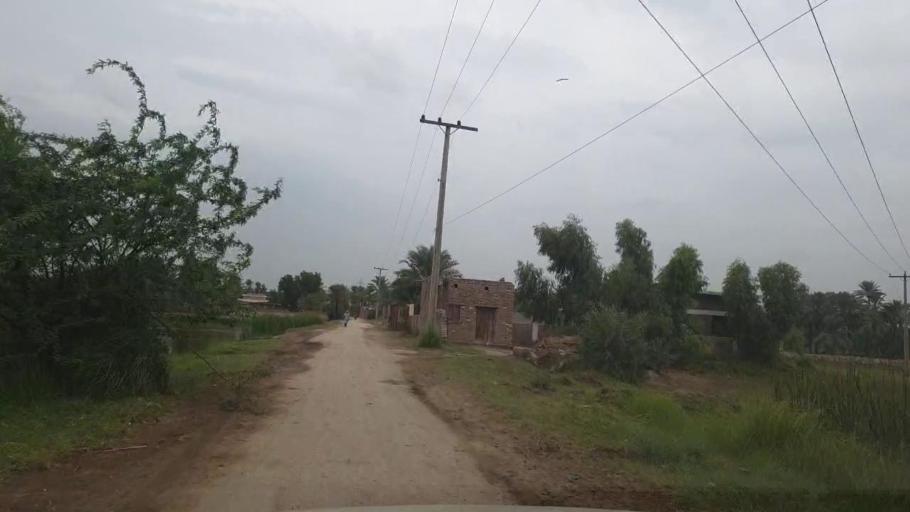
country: PK
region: Sindh
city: Khairpur
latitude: 27.5457
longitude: 68.7395
